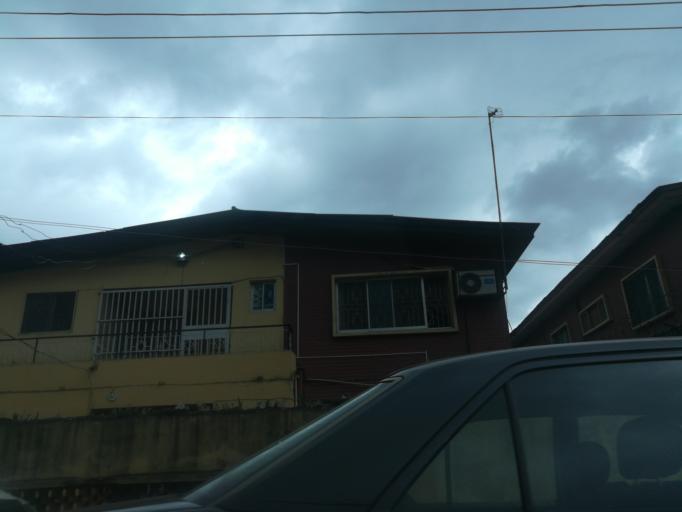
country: NG
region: Lagos
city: Ikeja
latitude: 6.6000
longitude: 3.3472
